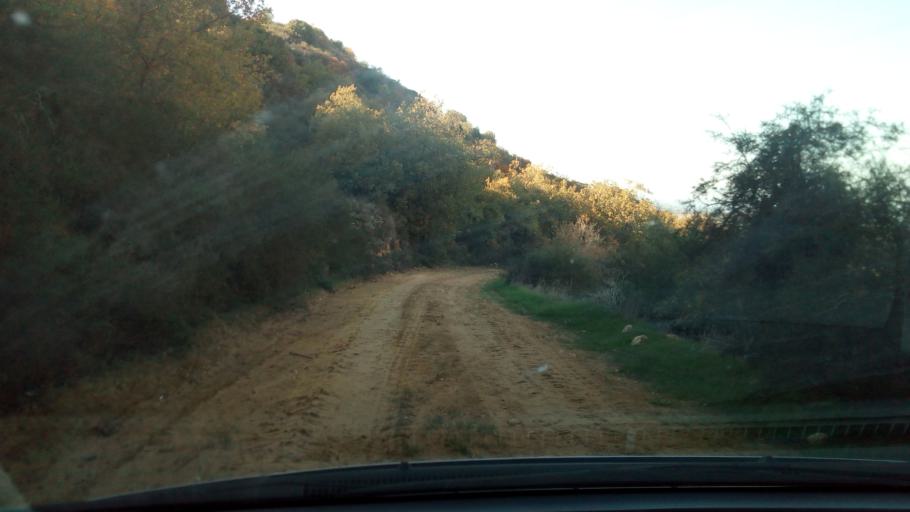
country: CY
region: Pafos
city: Polis
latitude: 34.9428
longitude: 32.4855
